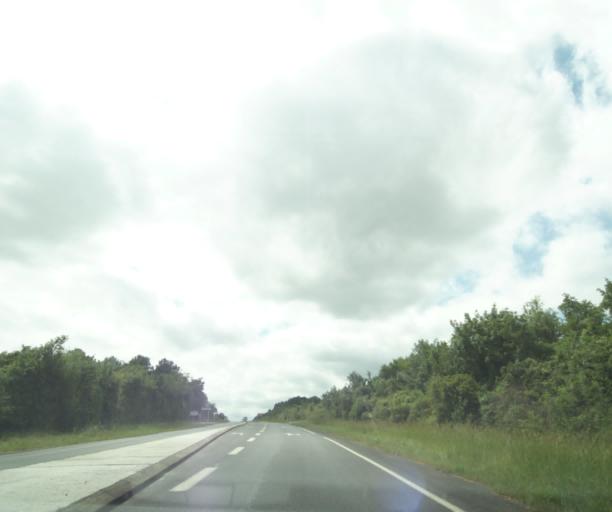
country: FR
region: Poitou-Charentes
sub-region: Departement des Deux-Sevres
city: Saint-Varent
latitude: 46.9141
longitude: -0.1958
